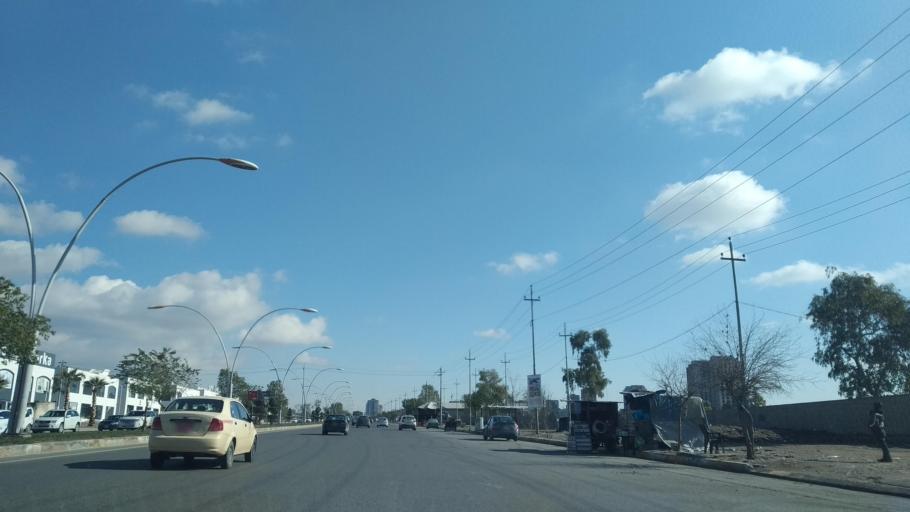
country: IQ
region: Arbil
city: Erbil
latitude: 36.2012
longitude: 44.0967
